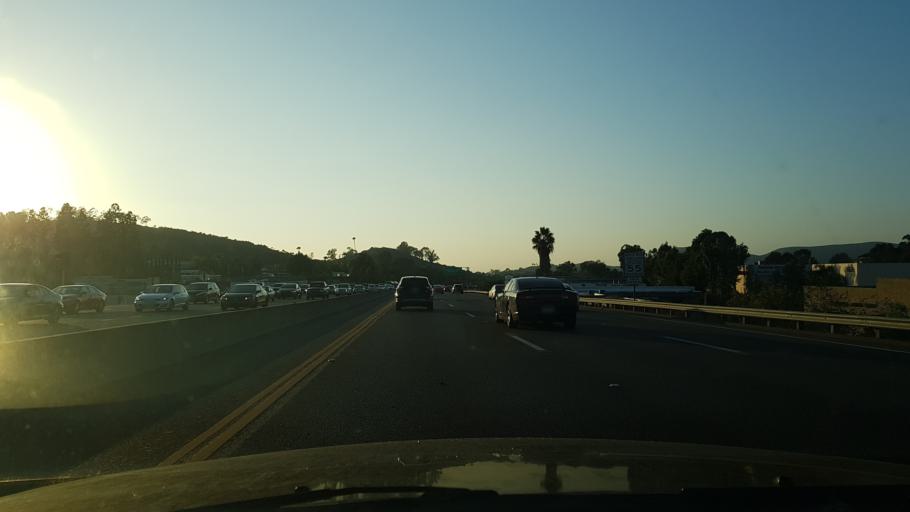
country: US
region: California
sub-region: San Diego County
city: San Marcos
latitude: 33.1351
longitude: -117.1309
